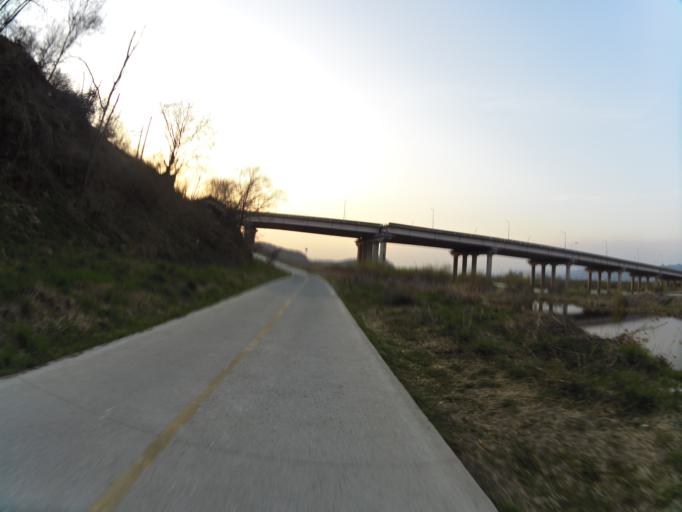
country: KR
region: Gyeongsangbuk-do
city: Gyeongsan-si
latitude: 35.8579
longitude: 128.6845
